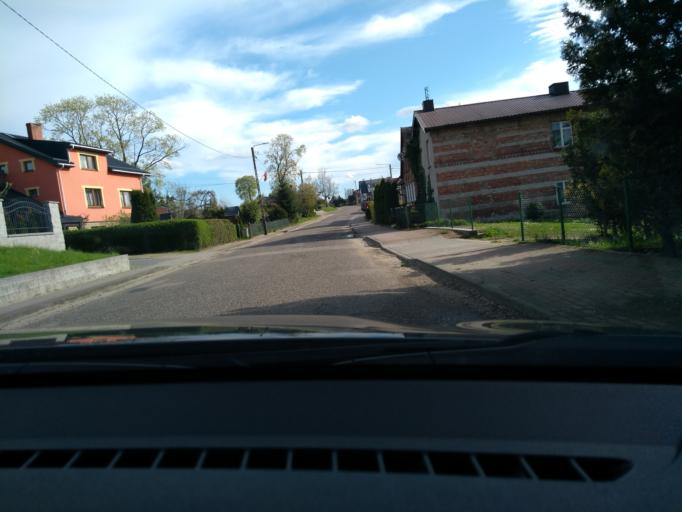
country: PL
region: Pomeranian Voivodeship
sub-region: Powiat leborski
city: Cewice
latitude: 54.3378
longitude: 17.6852
